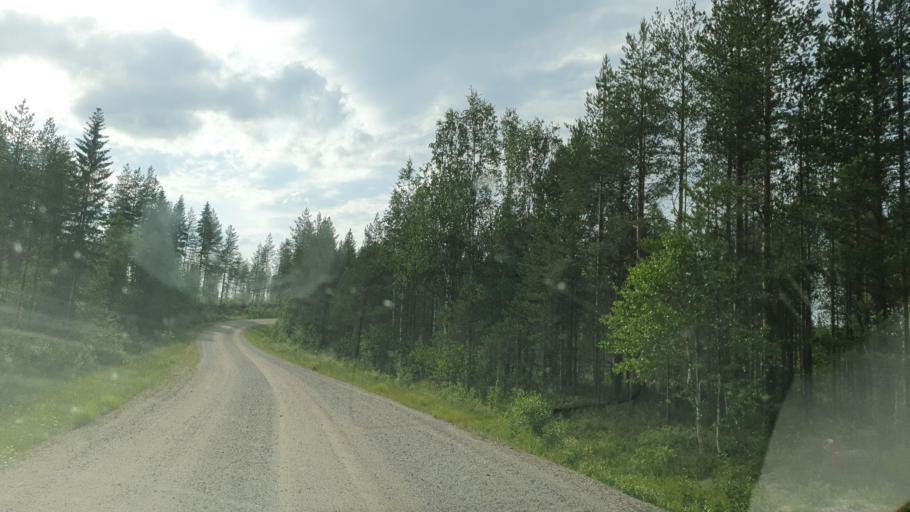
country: FI
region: Kainuu
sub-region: Kehys-Kainuu
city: Kuhmo
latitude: 64.0264
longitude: 29.8639
